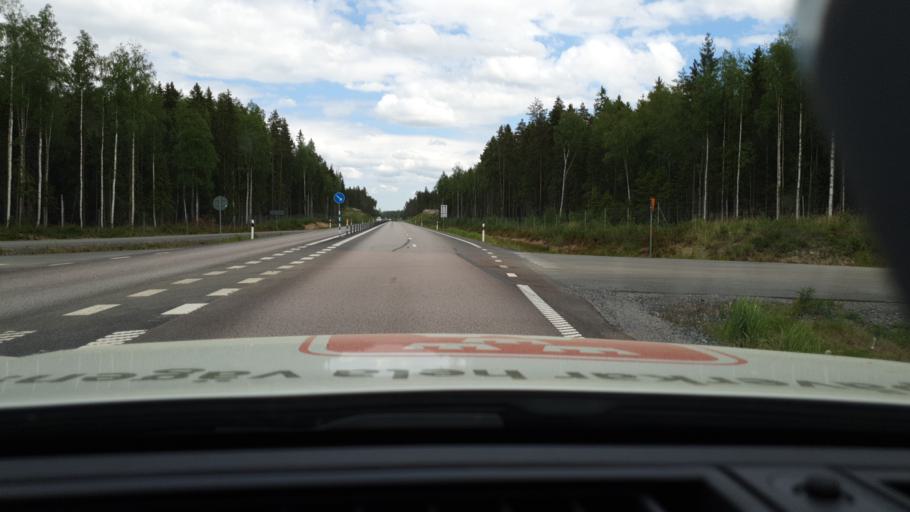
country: SE
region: Uppsala
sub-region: Heby Kommun
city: Tarnsjo
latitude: 60.0624
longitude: 16.8998
